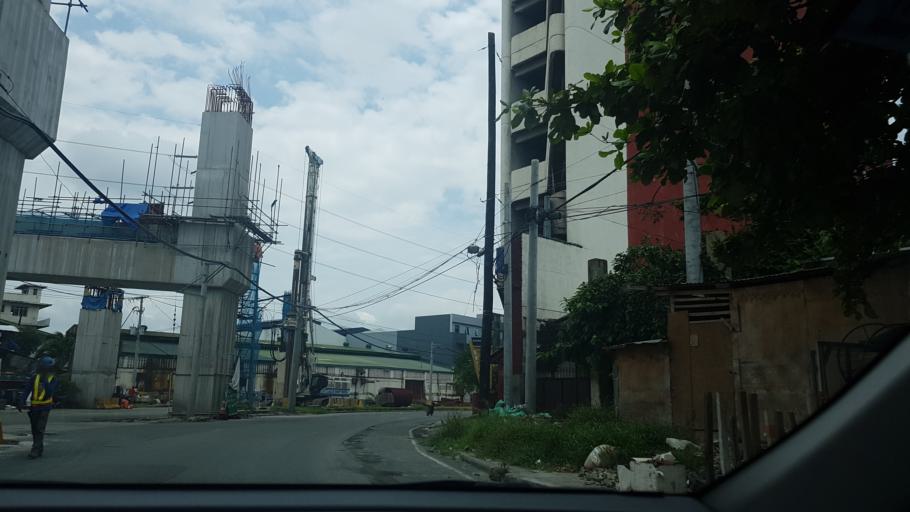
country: PH
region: Calabarzon
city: Del Monte
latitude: 14.6447
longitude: 121.0053
